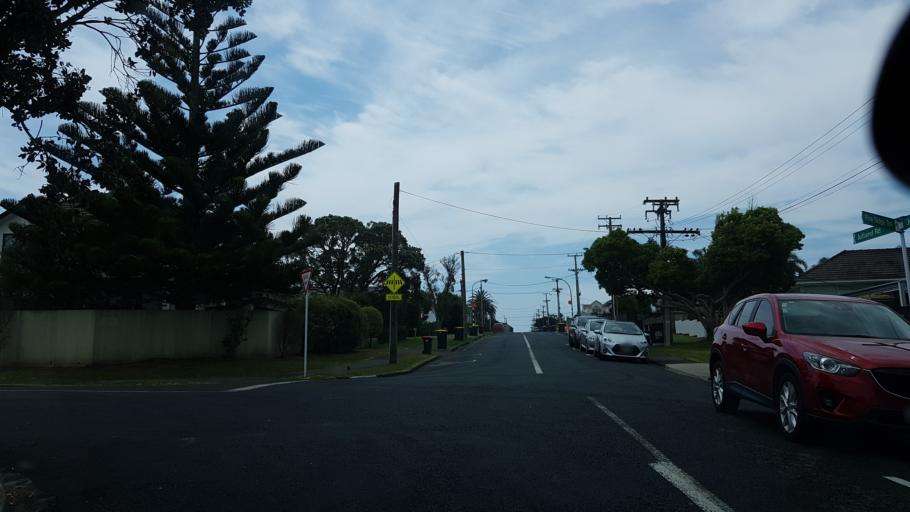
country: NZ
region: Auckland
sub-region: Auckland
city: North Shore
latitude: -36.8041
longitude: 174.7736
